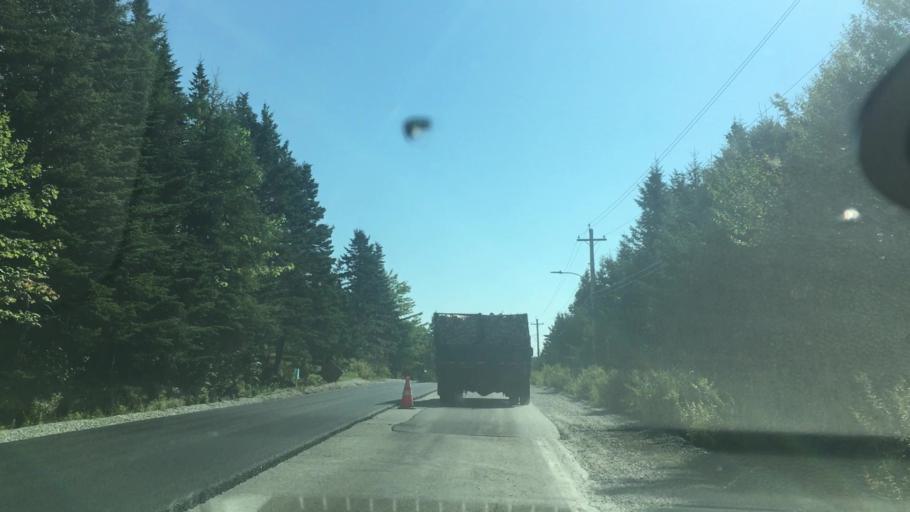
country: CA
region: Nova Scotia
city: New Glasgow
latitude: 44.9091
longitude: -62.5011
